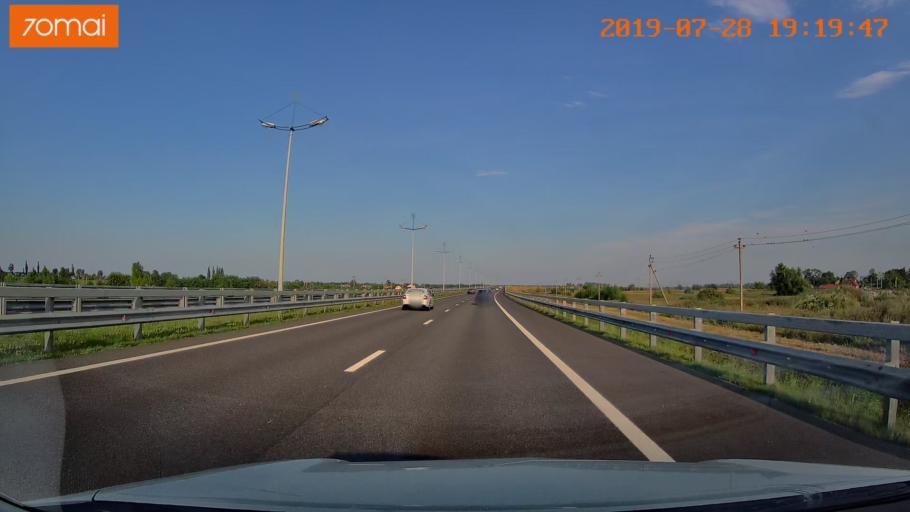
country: RU
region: Kaliningrad
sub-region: Zelenogradskiy Rayon
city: Zelenogradsk
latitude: 54.9194
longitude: 20.4689
